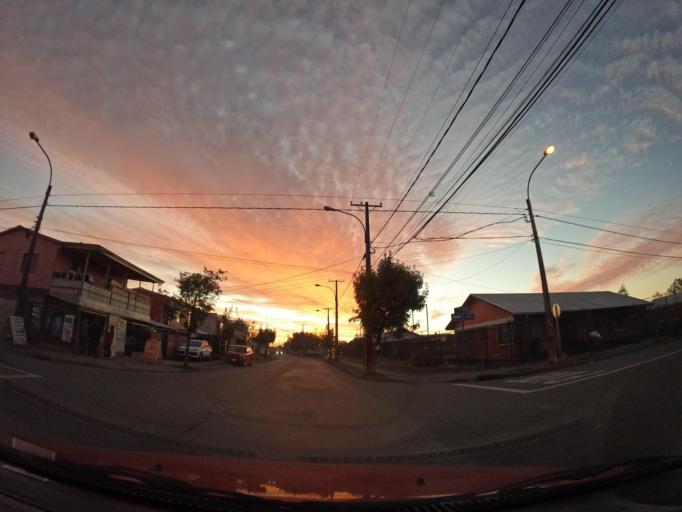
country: CL
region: Biobio
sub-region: Provincia de Nuble
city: Chillan
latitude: -36.6302
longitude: -72.0985
